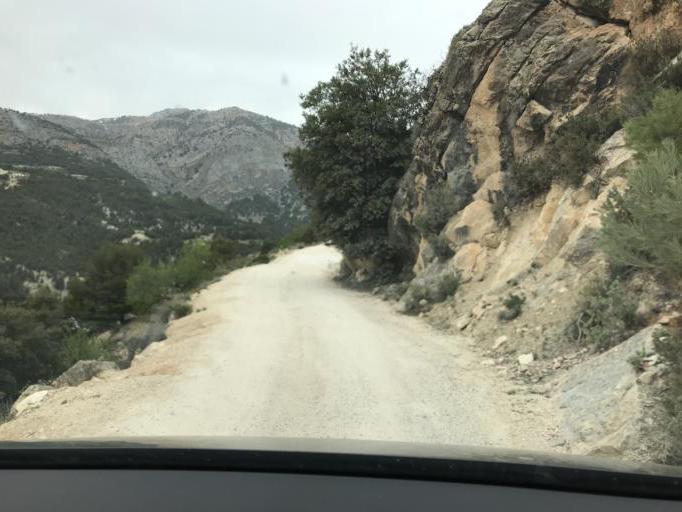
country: ES
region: Andalusia
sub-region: Provincia de Granada
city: Castril
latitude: 37.8246
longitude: -2.7717
